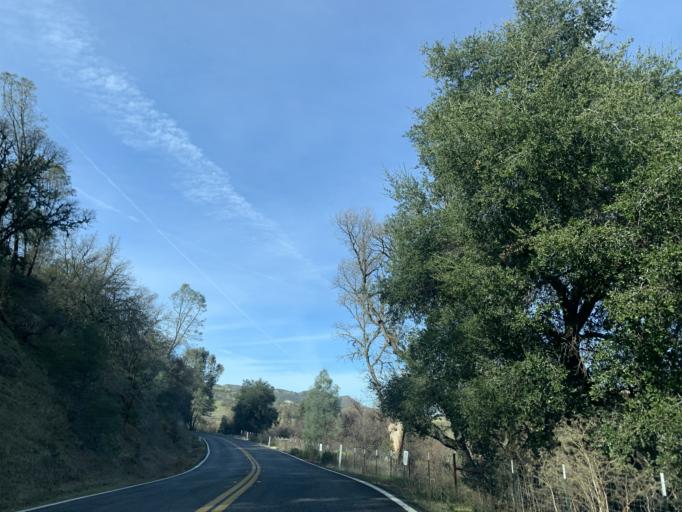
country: US
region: California
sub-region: Monterey County
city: Soledad
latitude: 36.5517
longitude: -121.1609
